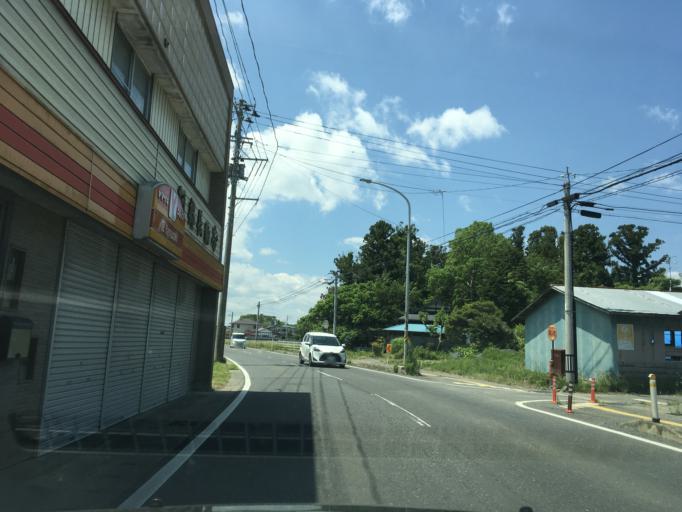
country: JP
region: Miyagi
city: Wakuya
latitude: 38.6764
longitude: 141.2502
